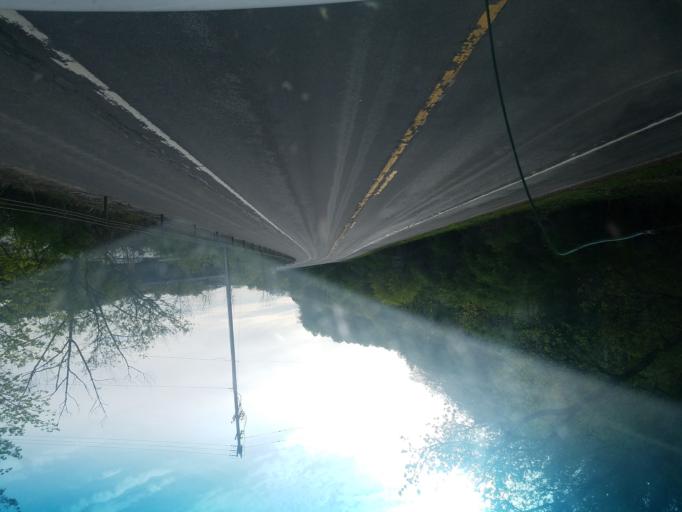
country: US
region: New York
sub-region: Herkimer County
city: Little Falls
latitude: 43.0362
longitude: -74.8404
